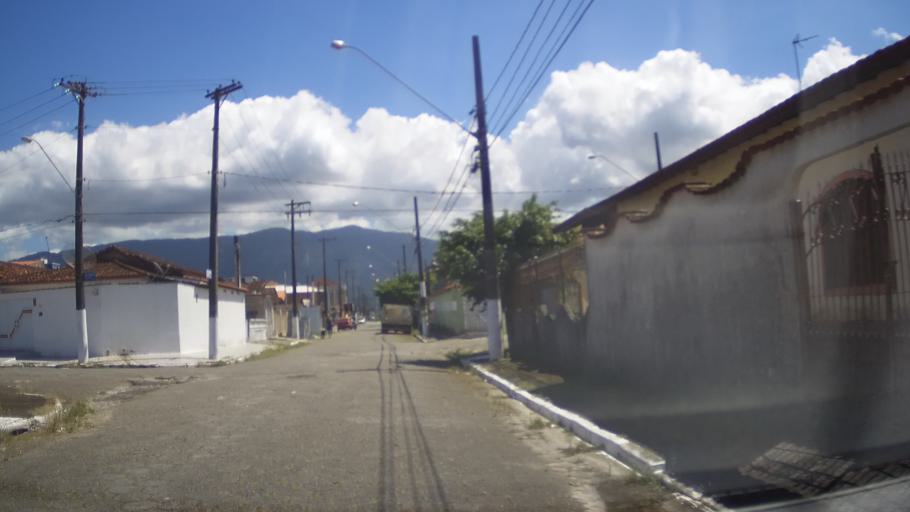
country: BR
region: Sao Paulo
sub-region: Mongagua
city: Mongagua
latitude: -24.0457
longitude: -46.5232
